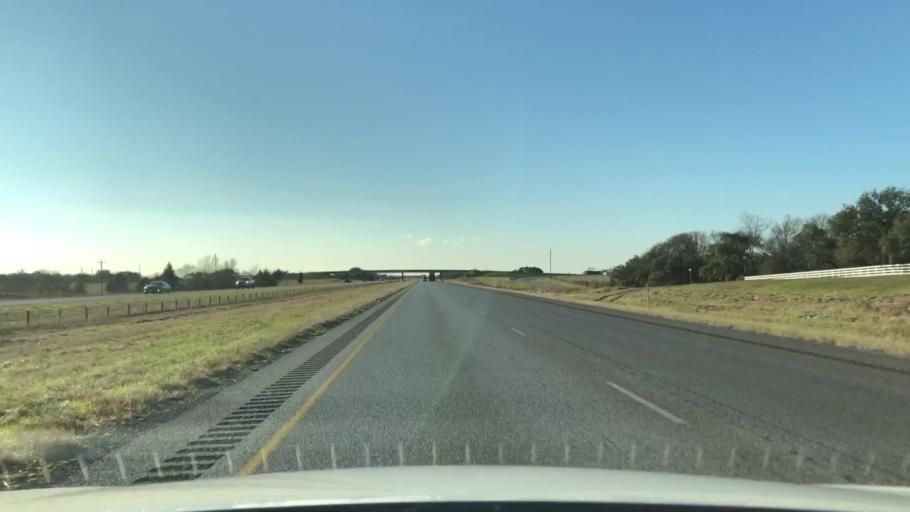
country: US
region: Texas
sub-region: Fayette County
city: Schulenburg
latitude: 29.6894
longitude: -96.9619
